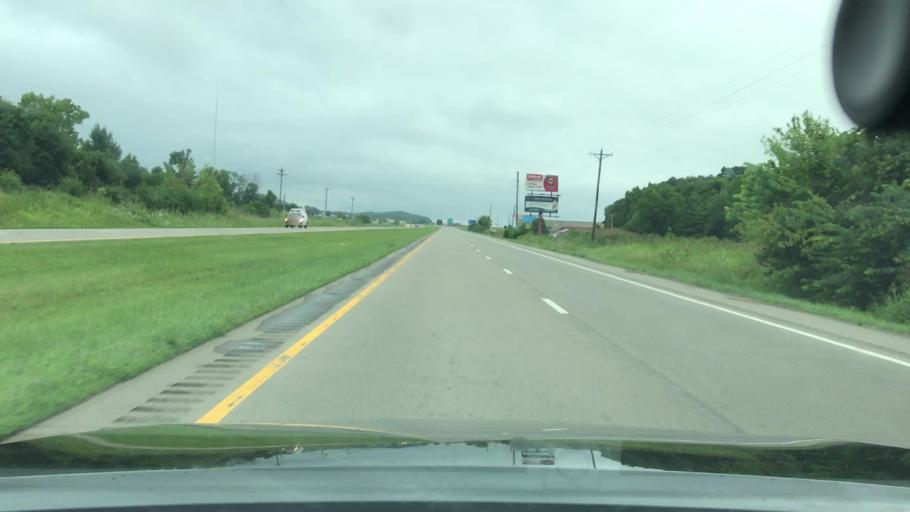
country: US
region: Ohio
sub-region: Ross County
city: Chillicothe
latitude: 39.4045
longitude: -82.9746
